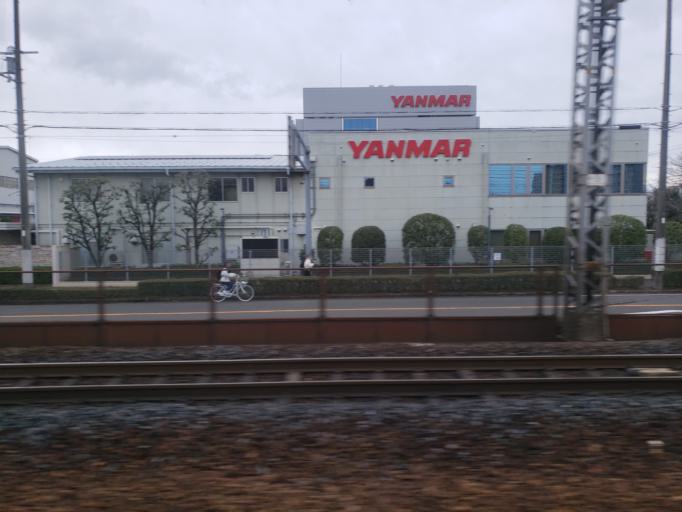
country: JP
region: Hyogo
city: Amagasaki
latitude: 34.7310
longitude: 135.4358
